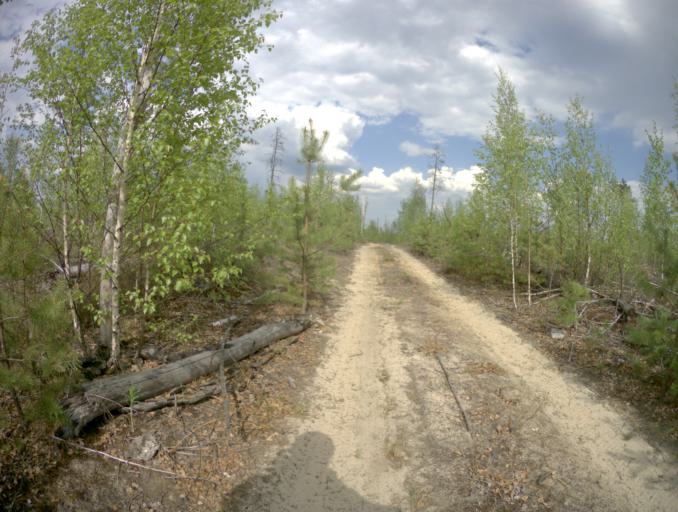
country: RU
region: Ivanovo
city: Talitsy
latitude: 56.4473
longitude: 42.2438
